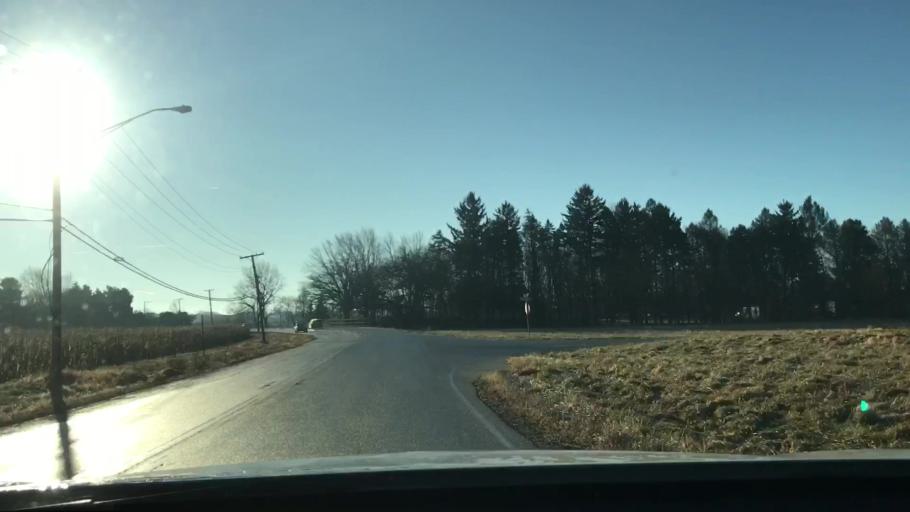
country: US
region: Illinois
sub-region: Kane County
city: Pingree Grove
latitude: 42.0919
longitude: -88.3989
